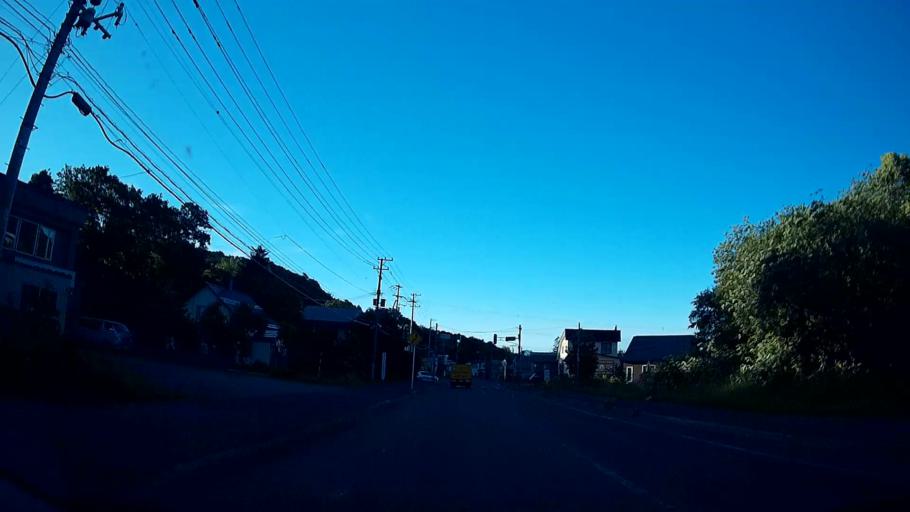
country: JP
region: Hokkaido
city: Otaru
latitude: 43.1549
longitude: 141.0416
